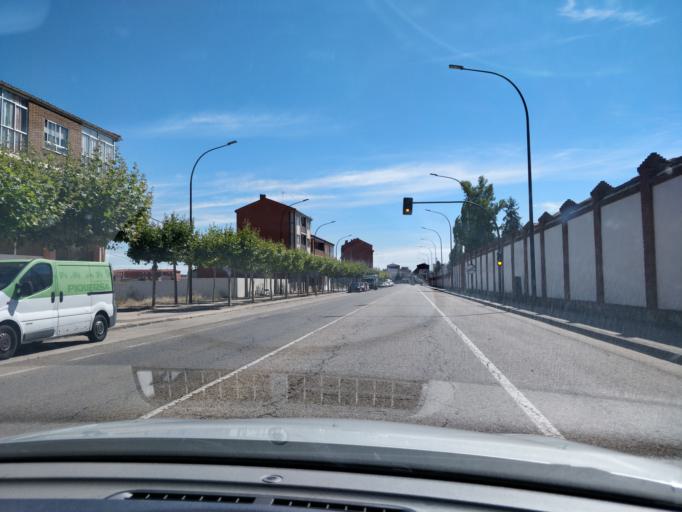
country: ES
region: Castille and Leon
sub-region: Provincia de Leon
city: Astorga
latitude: 42.4620
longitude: -6.0682
